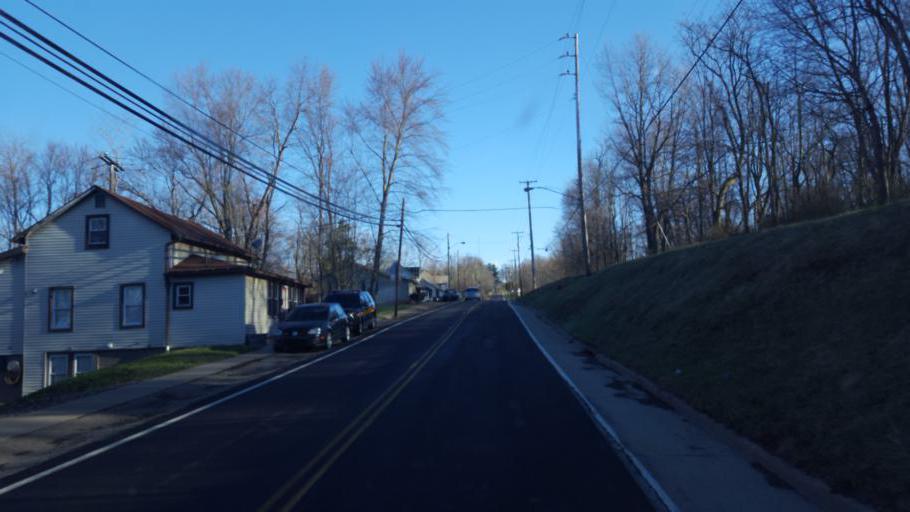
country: US
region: Ohio
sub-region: Holmes County
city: Millersburg
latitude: 40.5576
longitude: -81.9121
